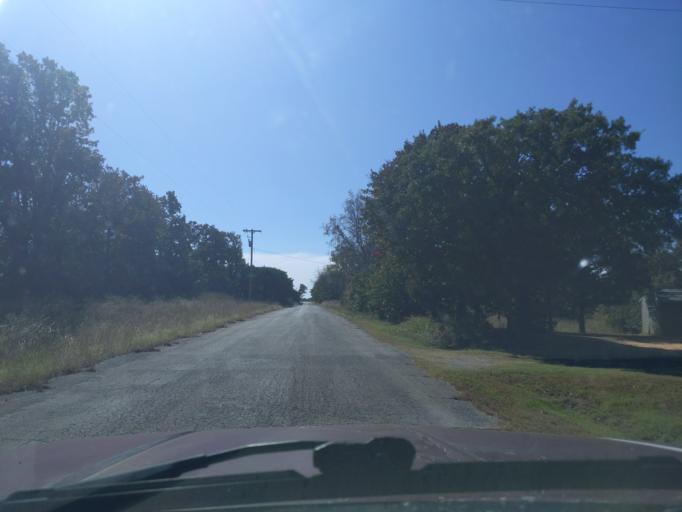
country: US
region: Oklahoma
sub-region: Creek County
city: Bristow
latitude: 35.7010
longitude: -96.4098
